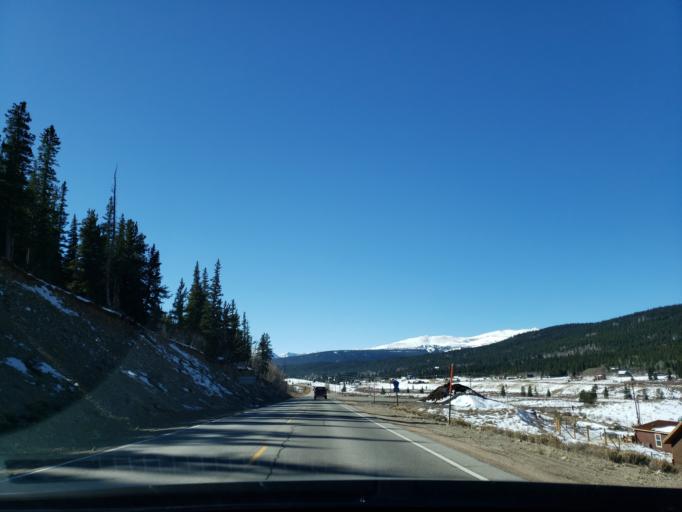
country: US
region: Colorado
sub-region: Park County
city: Fairplay
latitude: 39.3146
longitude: -106.0581
